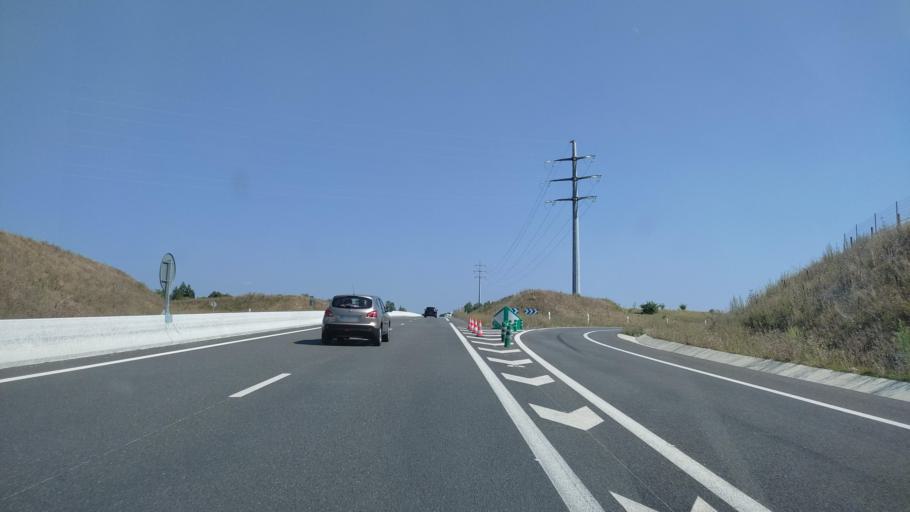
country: FR
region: Poitou-Charentes
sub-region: Departement de la Charente
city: Balzac
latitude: 45.6924
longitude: 0.0986
